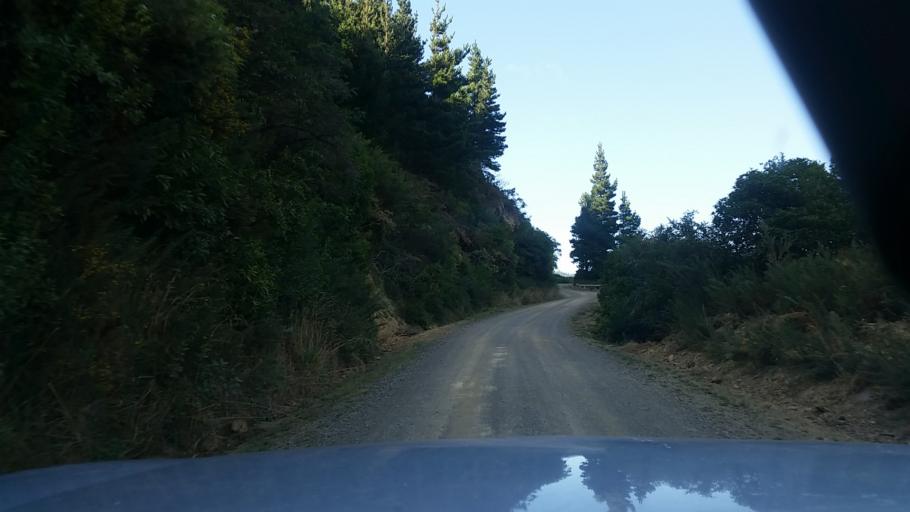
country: NZ
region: Marlborough
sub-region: Marlborough District
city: Picton
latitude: -41.2895
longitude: 174.1670
